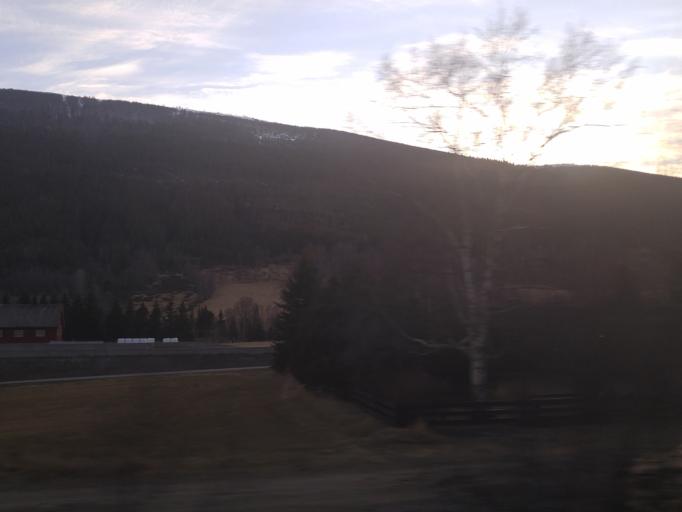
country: NO
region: Oppland
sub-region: Dovre
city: Dovre
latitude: 61.9667
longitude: 9.2538
